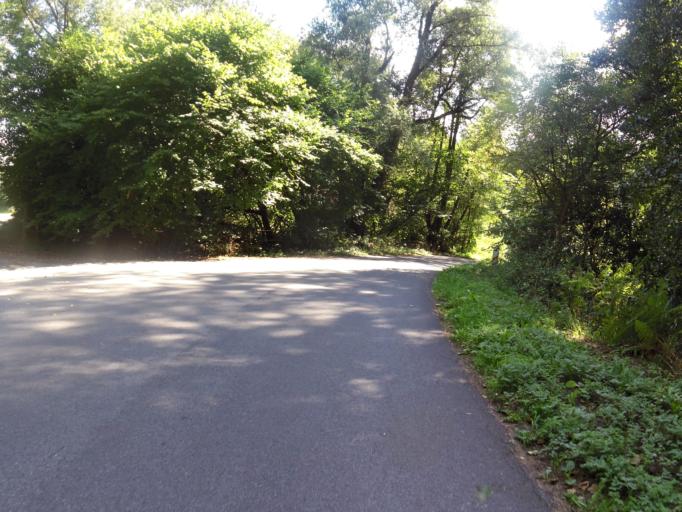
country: DE
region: North Rhine-Westphalia
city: Stolberg
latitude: 50.7922
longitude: 6.2000
